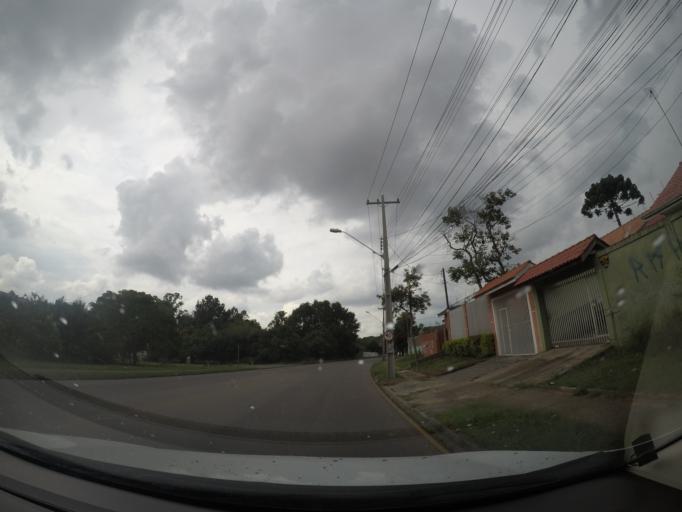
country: BR
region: Parana
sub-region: Sao Jose Dos Pinhais
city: Sao Jose dos Pinhais
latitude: -25.5249
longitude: -49.2492
